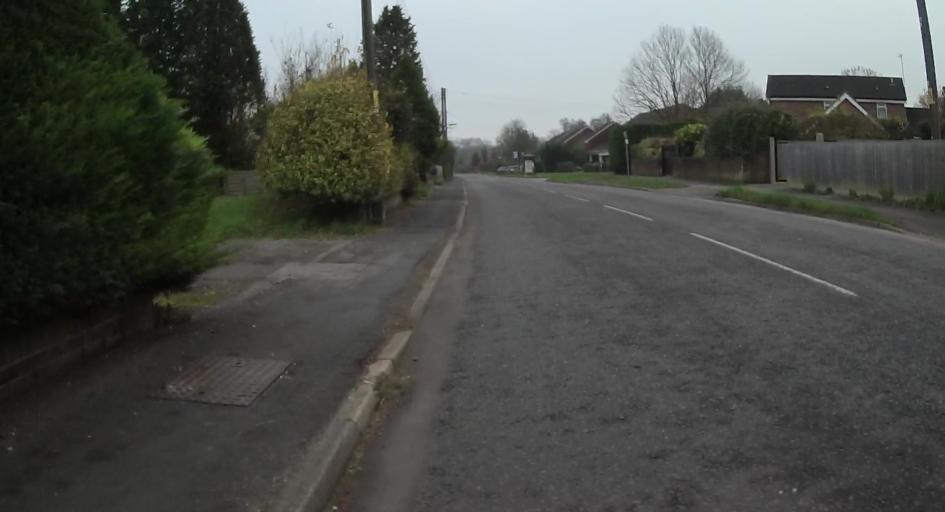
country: GB
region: England
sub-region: Hampshire
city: Kings Worthy
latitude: 51.1033
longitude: -1.3051
